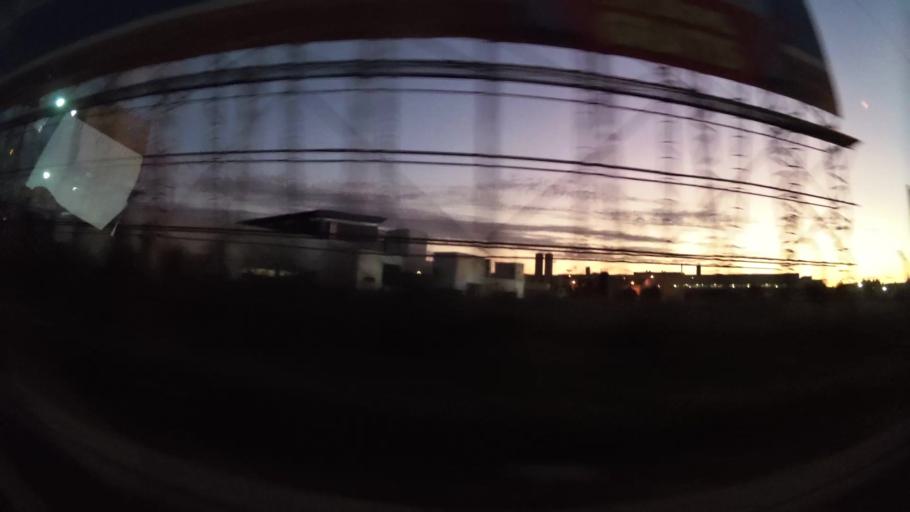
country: AR
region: Buenos Aires
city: Santa Catalina - Dique Lujan
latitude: -34.4556
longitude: -58.7278
